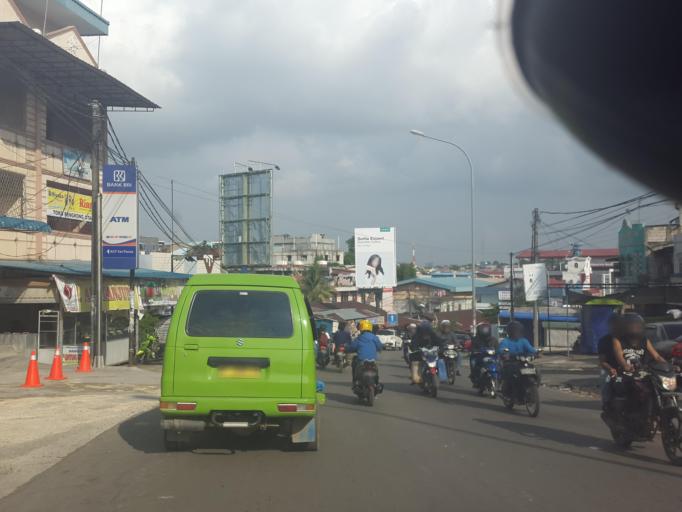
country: SG
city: Singapore
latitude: 1.1503
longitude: 104.0257
